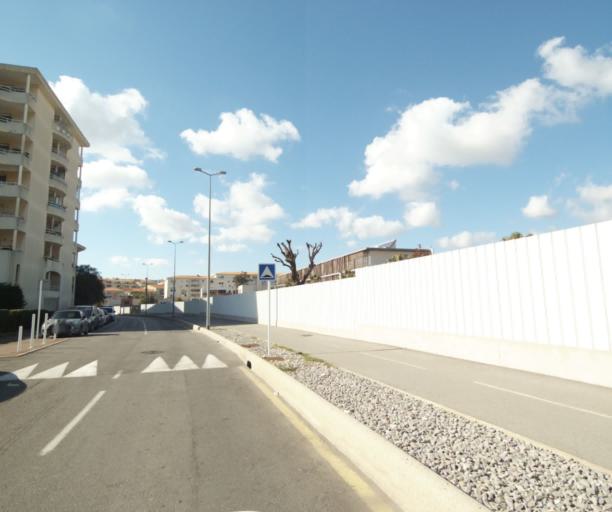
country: FR
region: Provence-Alpes-Cote d'Azur
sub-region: Departement des Alpes-Maritimes
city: Antibes
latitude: 43.5735
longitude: 7.0941
